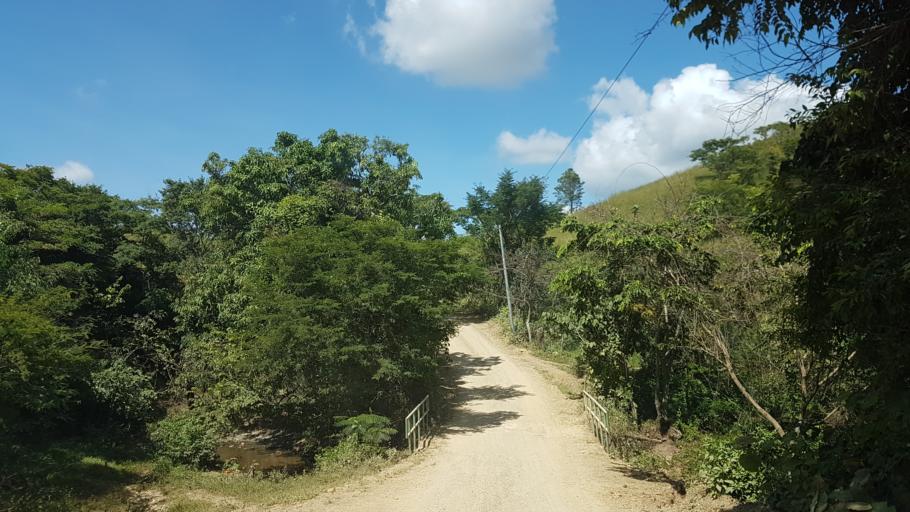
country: HN
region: El Paraiso
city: Santa Cruz
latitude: 13.7321
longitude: -86.6912
